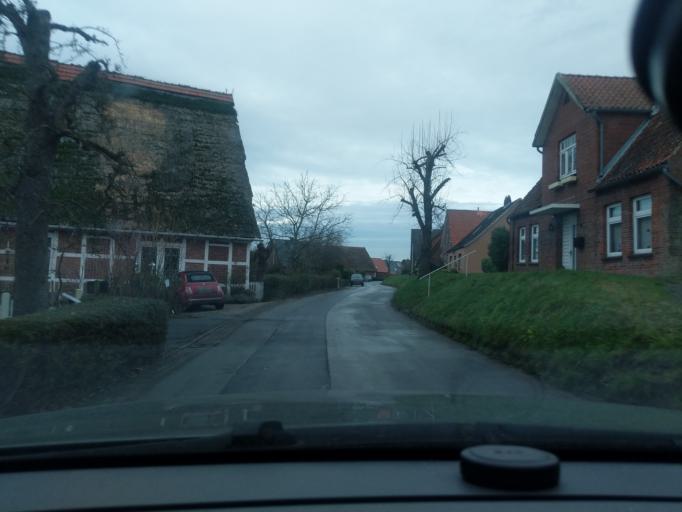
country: DE
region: Lower Saxony
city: Neuenkirchen
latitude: 53.5298
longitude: 9.6058
